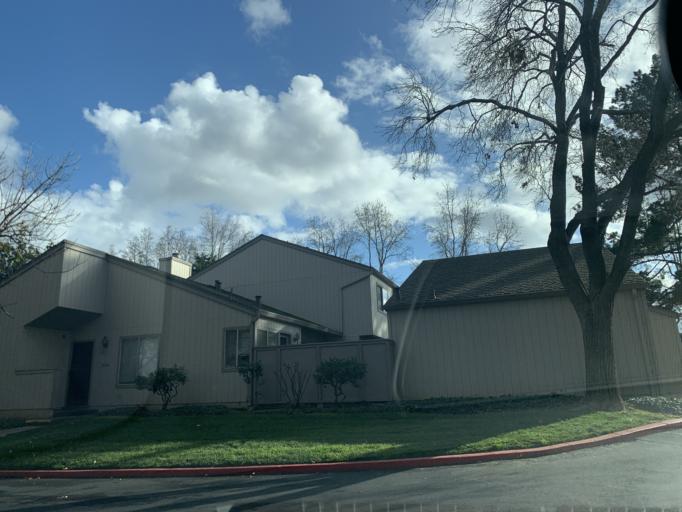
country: US
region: California
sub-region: Santa Clara County
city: Buena Vista
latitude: 37.3077
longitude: -121.9175
